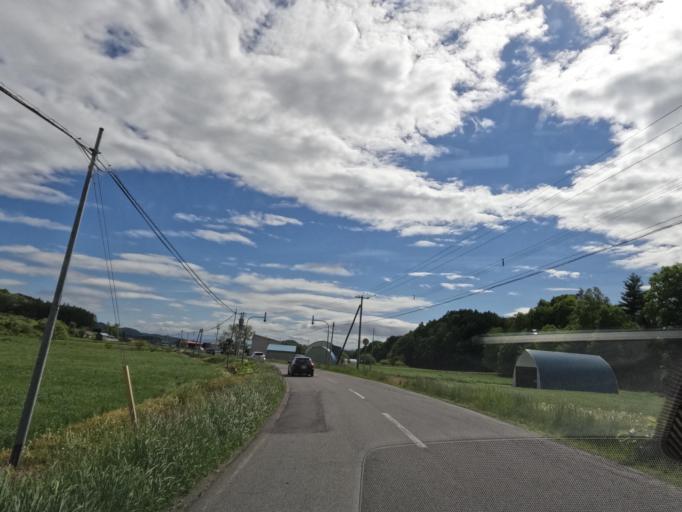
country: JP
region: Hokkaido
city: Kamikawa
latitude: 43.8681
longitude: 142.5646
